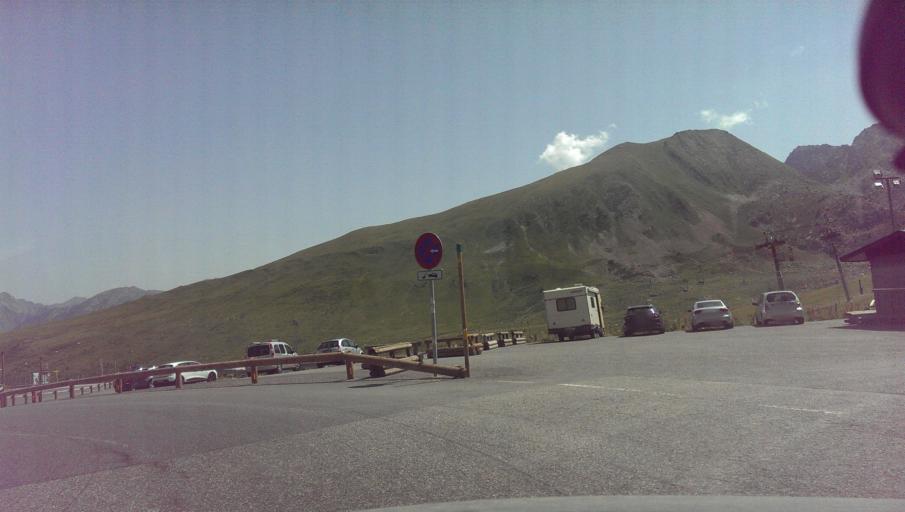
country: AD
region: Encamp
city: Pas de la Casa
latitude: 42.5374
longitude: 1.7269
